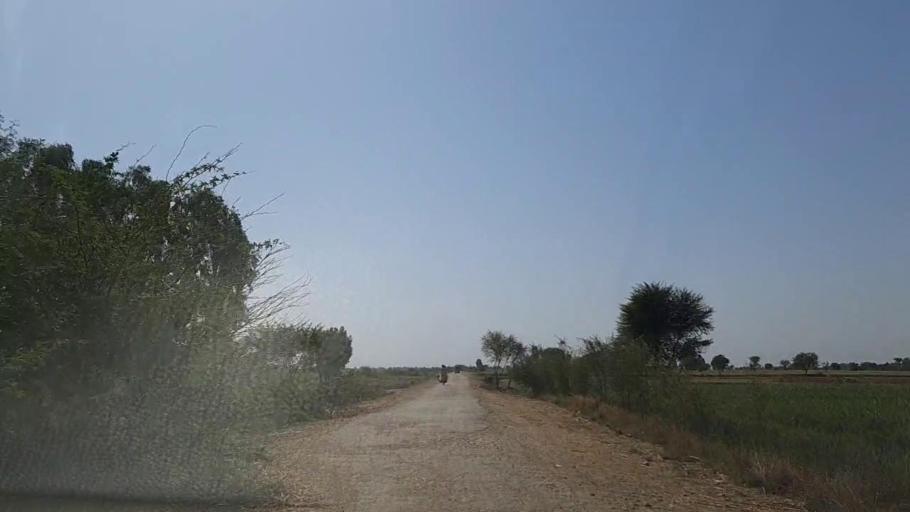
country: PK
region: Sindh
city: Samaro
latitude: 25.2385
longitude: 69.4106
